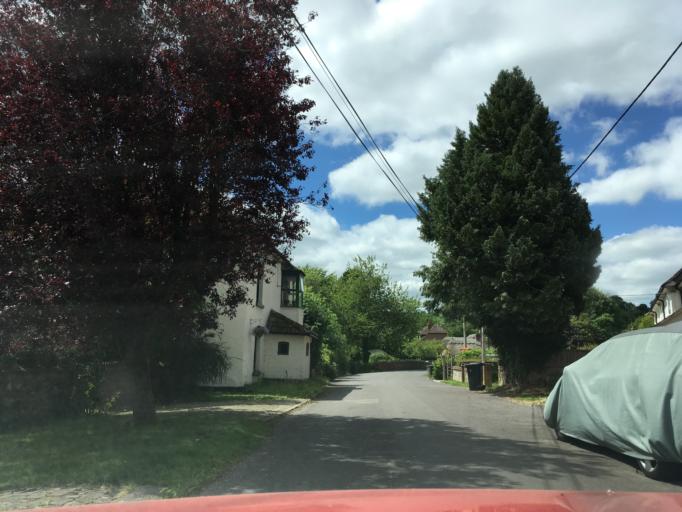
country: GB
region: England
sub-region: Hampshire
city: Highclere
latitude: 51.2650
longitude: -1.4229
